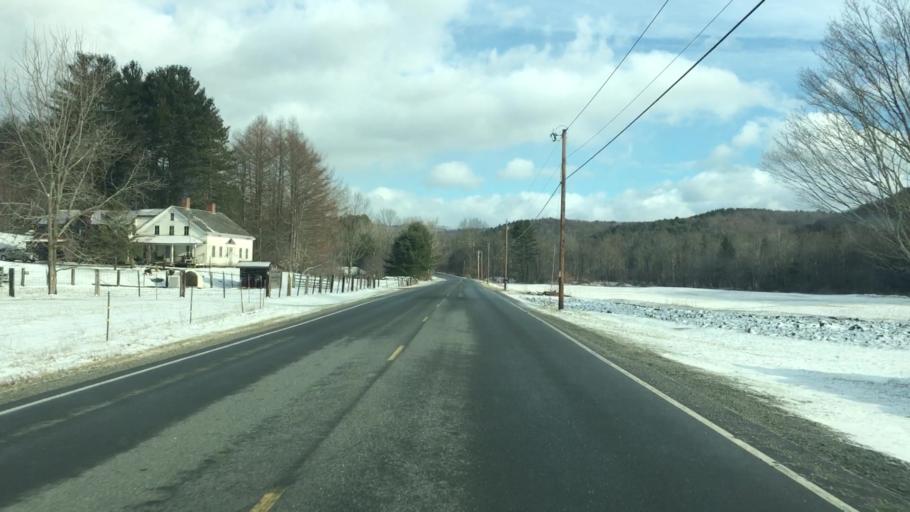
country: US
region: Massachusetts
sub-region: Franklin County
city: Colrain
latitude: 42.7142
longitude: -72.7048
